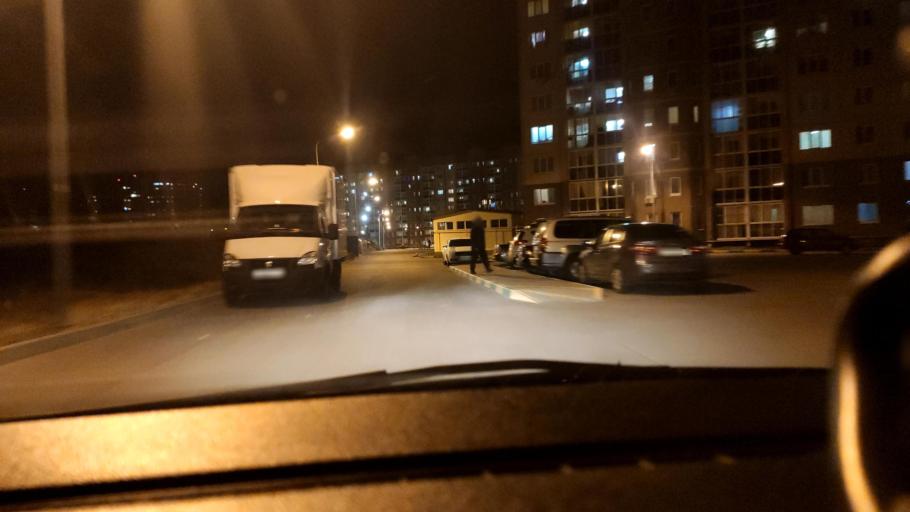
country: RU
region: Voronezj
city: Shilovo
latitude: 51.5721
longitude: 39.1290
